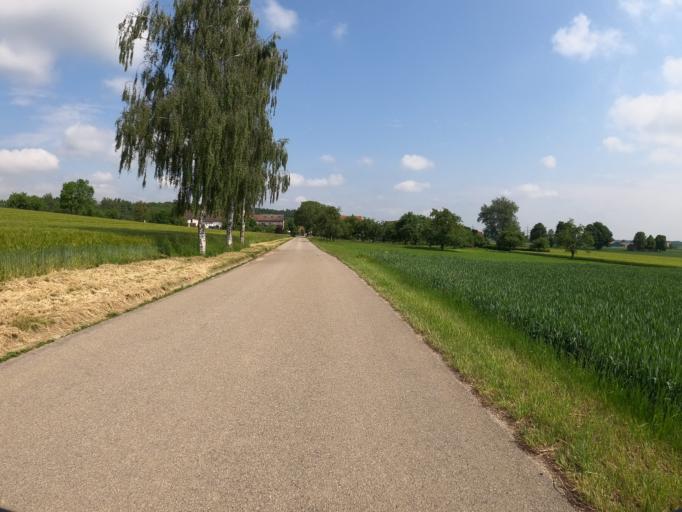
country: DE
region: Bavaria
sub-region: Swabia
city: Holzheim
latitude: 48.3586
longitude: 10.0995
